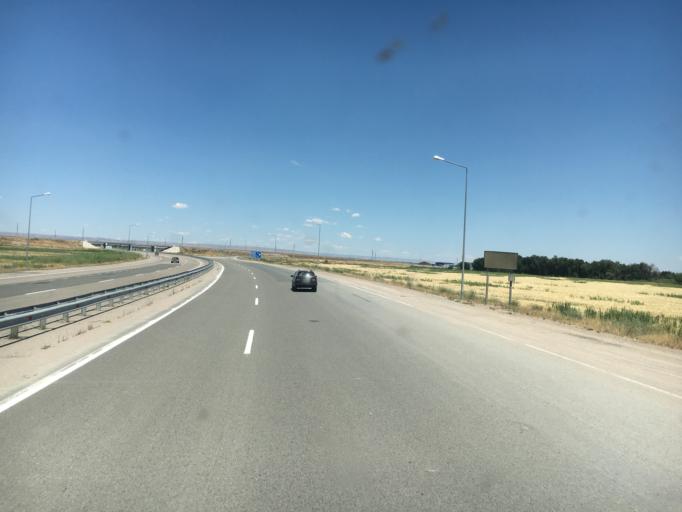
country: KG
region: Chuy
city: Sokuluk
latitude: 43.2703
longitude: 74.2255
